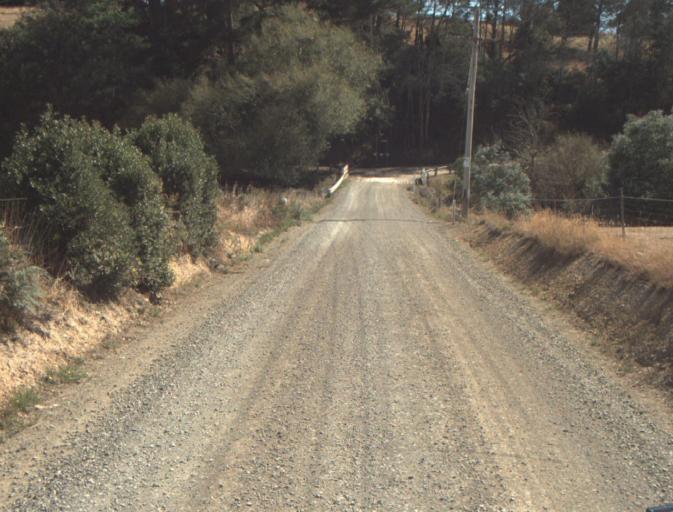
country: AU
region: Tasmania
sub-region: Launceston
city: Mayfield
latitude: -41.2240
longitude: 147.2371
